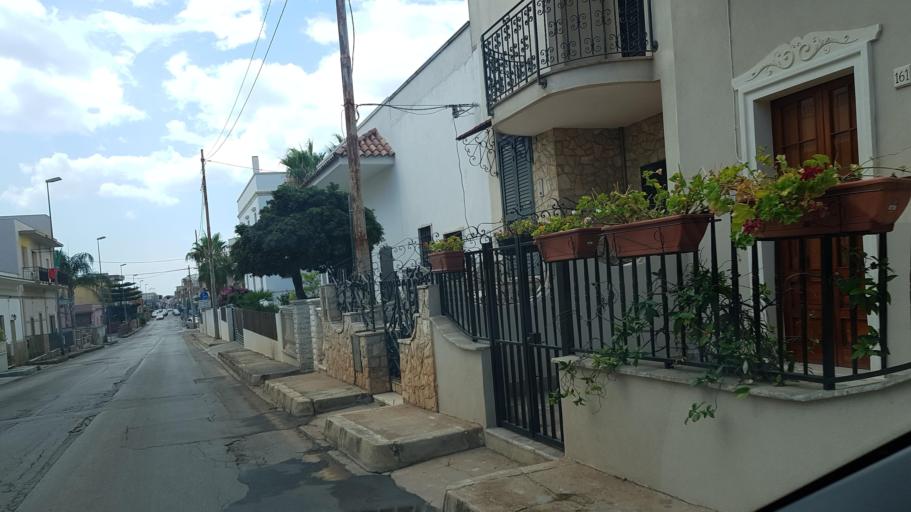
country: IT
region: Apulia
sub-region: Provincia di Lecce
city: Taurisano
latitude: 39.9585
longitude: 18.2215
